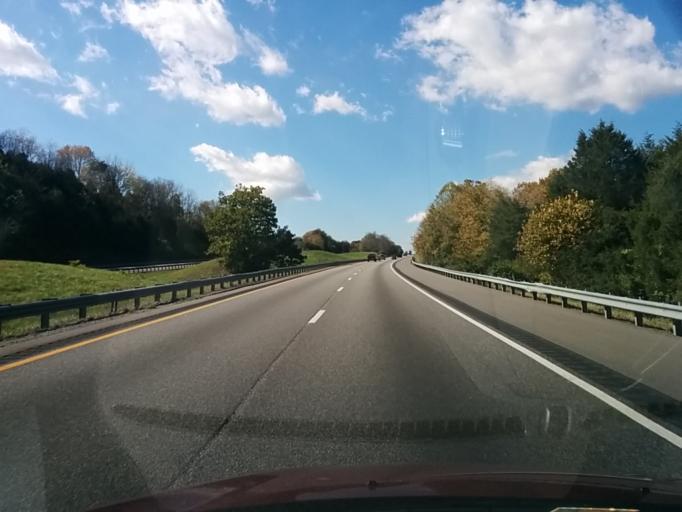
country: US
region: Virginia
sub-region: Botetourt County
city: Fincastle
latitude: 37.4653
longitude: -79.8180
